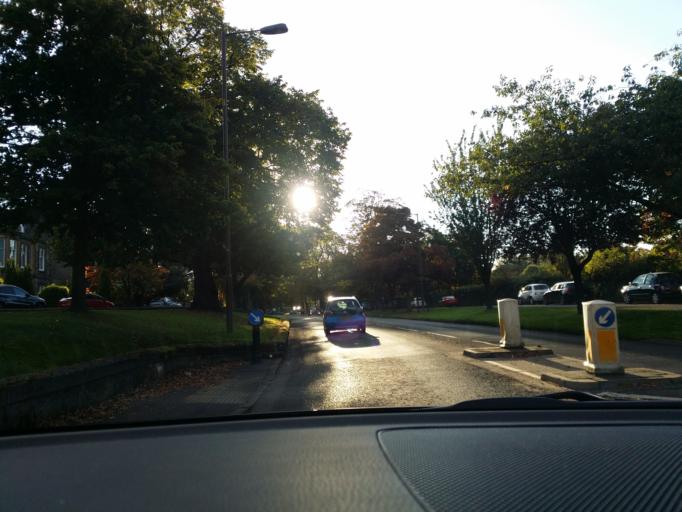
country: GB
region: Scotland
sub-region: Stirling
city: Stirling
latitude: 56.1133
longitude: -3.9455
